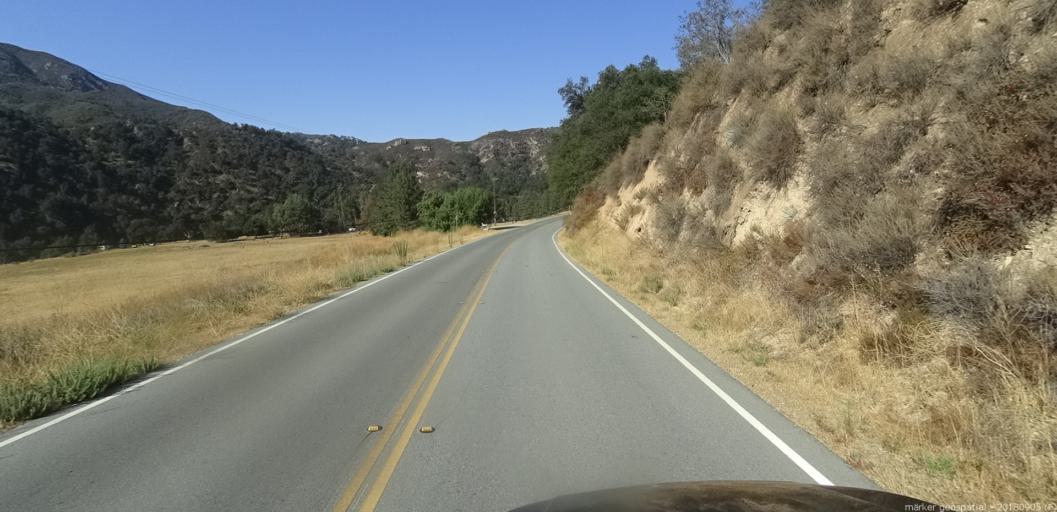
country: US
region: California
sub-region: Monterey County
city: Soledad
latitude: 36.2320
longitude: -121.4625
